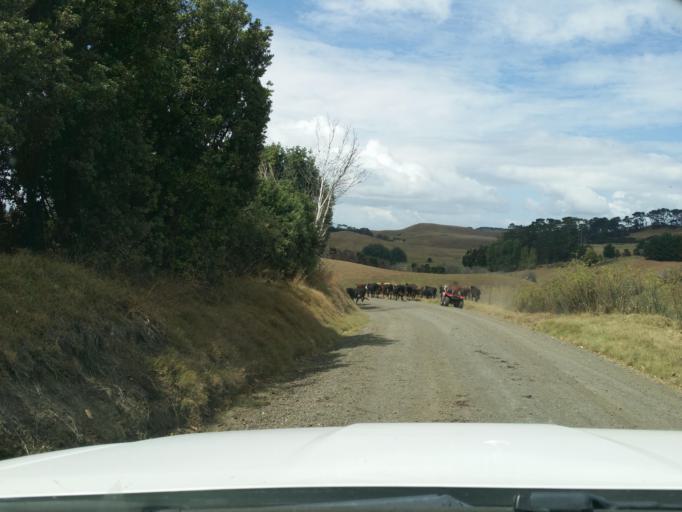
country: NZ
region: Auckland
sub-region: Auckland
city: Wellsford
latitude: -36.3379
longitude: 174.1595
